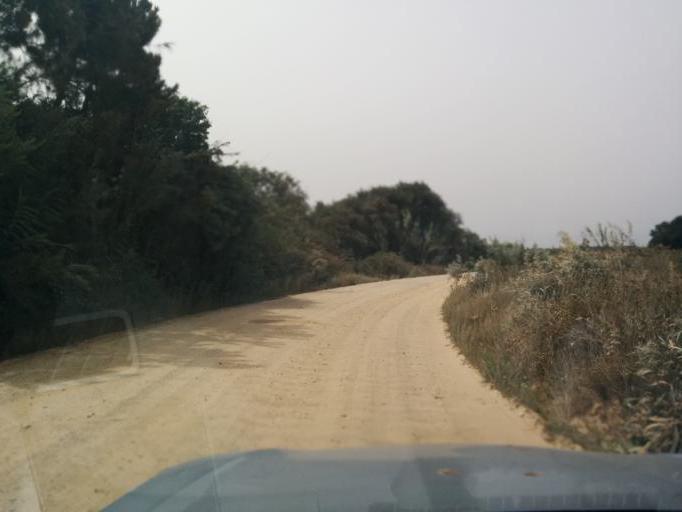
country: PT
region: Beja
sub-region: Odemira
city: Sao Teotonio
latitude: 37.5055
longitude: -8.7826
